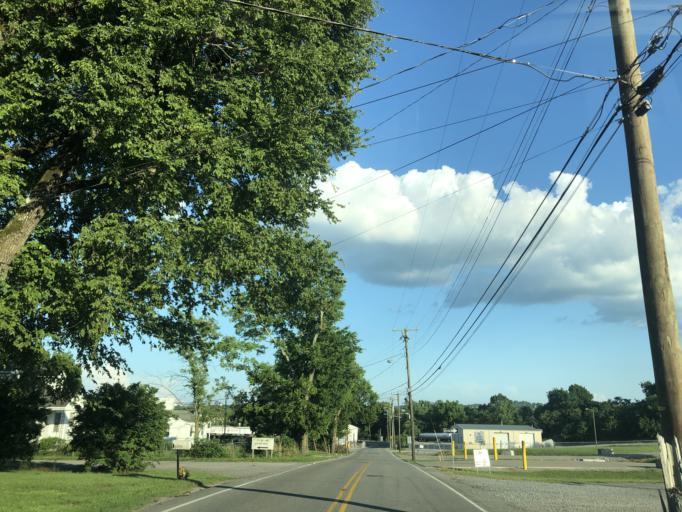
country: US
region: Tennessee
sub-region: Davidson County
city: Nashville
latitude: 36.1856
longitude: -86.8351
